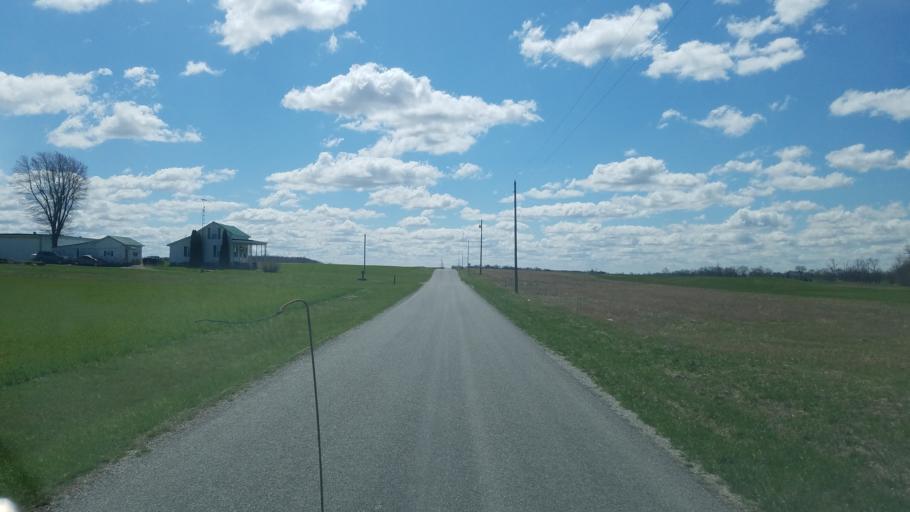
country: US
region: Ohio
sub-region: Hancock County
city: Findlay
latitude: 41.0621
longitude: -83.5148
